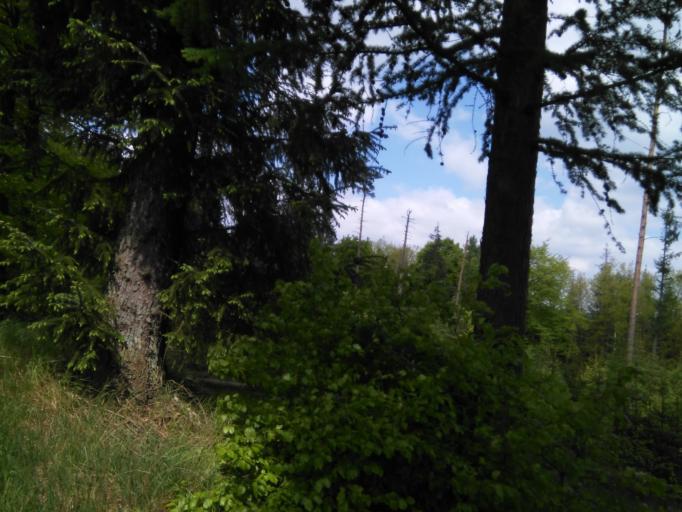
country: DK
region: Central Jutland
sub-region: Silkeborg Kommune
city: Svejbaek
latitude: 56.0619
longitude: 9.6241
